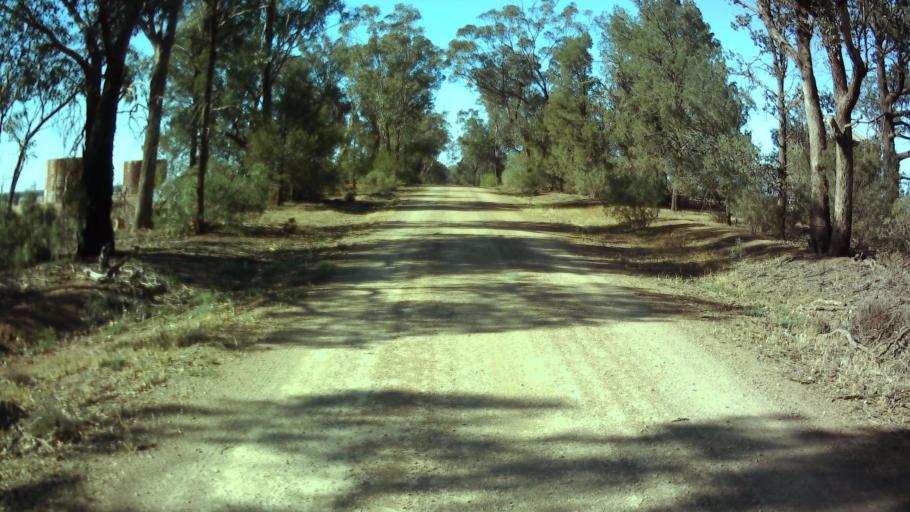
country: AU
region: New South Wales
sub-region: Weddin
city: Grenfell
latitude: -33.9089
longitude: 147.8771
